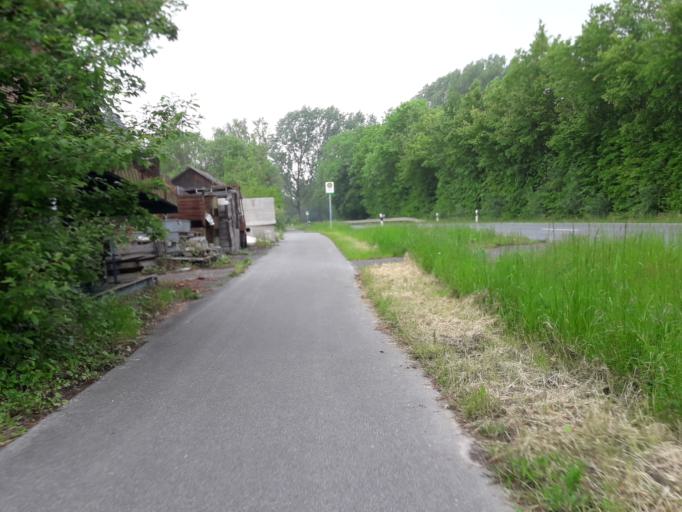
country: DE
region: North Rhine-Westphalia
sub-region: Regierungsbezirk Detmold
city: Salzkotten
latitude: 51.6527
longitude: 8.6550
